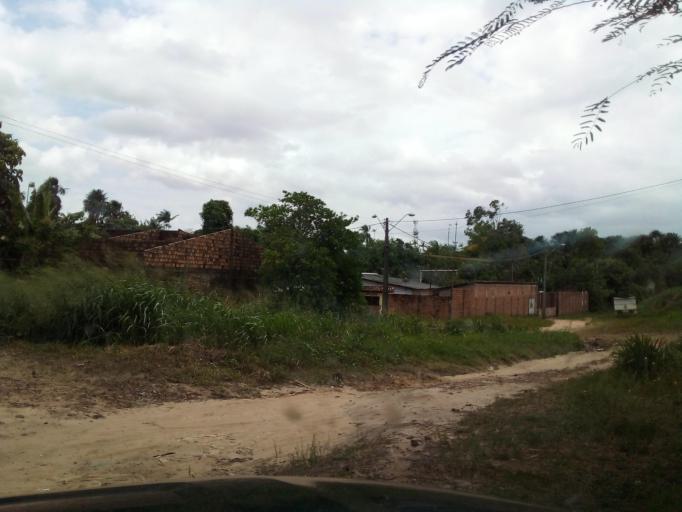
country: BR
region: Maranhao
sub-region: Sao Luis
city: Sao Luis
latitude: -2.6963
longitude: -44.3074
